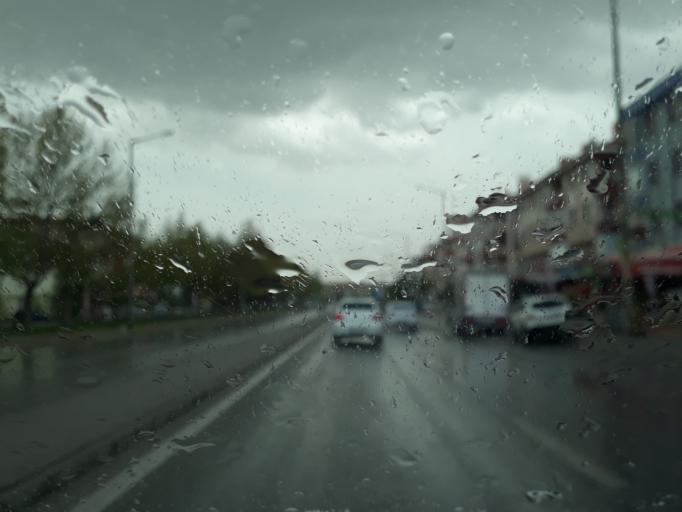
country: TR
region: Konya
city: Selcuklu
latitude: 37.9194
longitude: 32.4926
